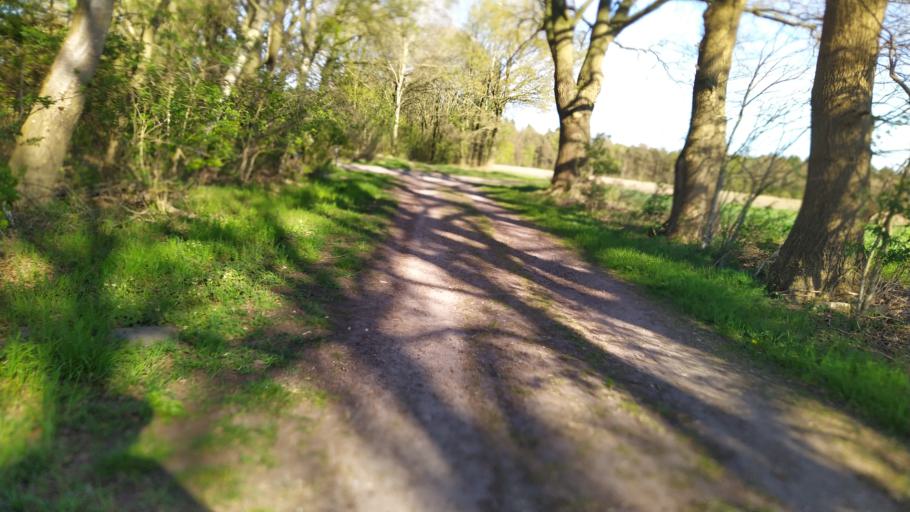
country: DE
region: Lower Saxony
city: Klein Meckelsen
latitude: 53.2941
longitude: 9.4599
